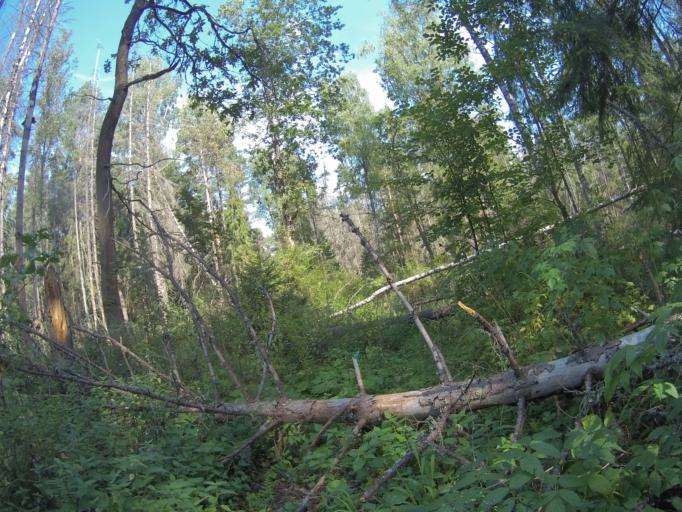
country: RU
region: Vladimir
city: Kommunar
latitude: 56.1002
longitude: 40.5117
